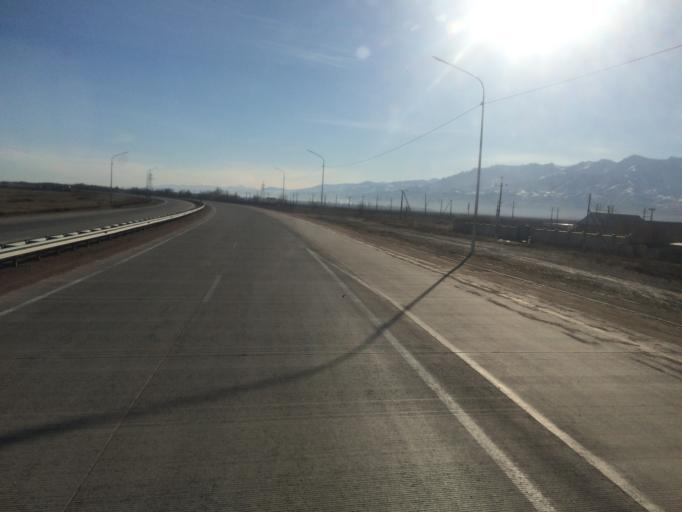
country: KG
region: Talas
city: Ivanovo-Alekseyevka
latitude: 42.9907
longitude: 72.1155
